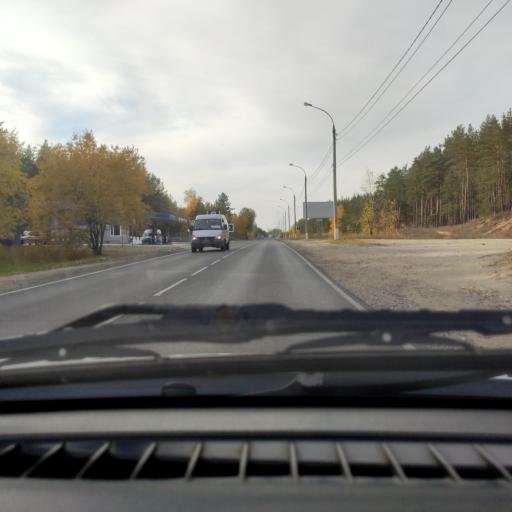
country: RU
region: Samara
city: Zhigulevsk
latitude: 53.4772
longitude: 49.4502
